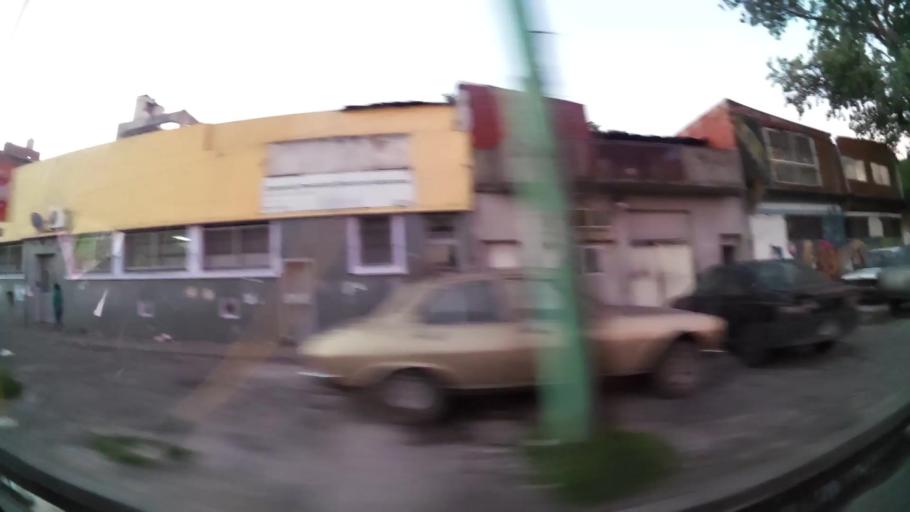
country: AR
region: Buenos Aires F.D.
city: Villa Lugano
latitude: -34.6499
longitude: -58.4310
